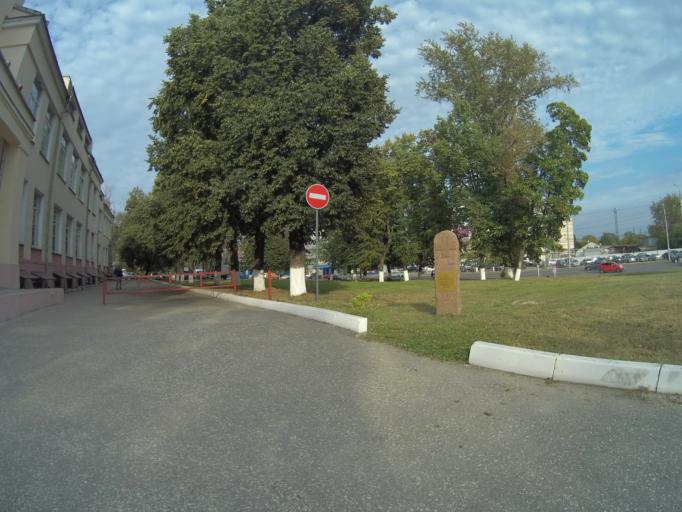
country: RU
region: Vladimir
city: Kommunar
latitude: 56.1382
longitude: 40.4320
